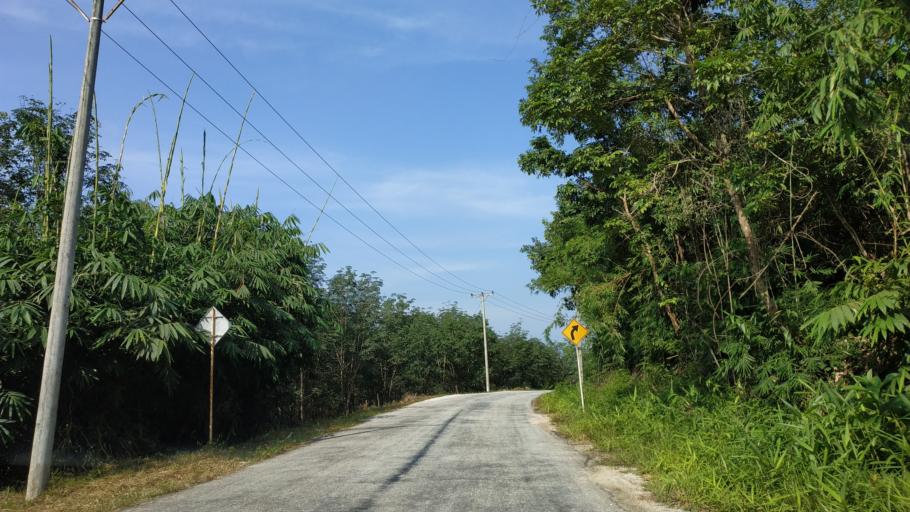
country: MM
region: Tanintharyi
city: Dawei
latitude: 14.5982
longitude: 98.0868
